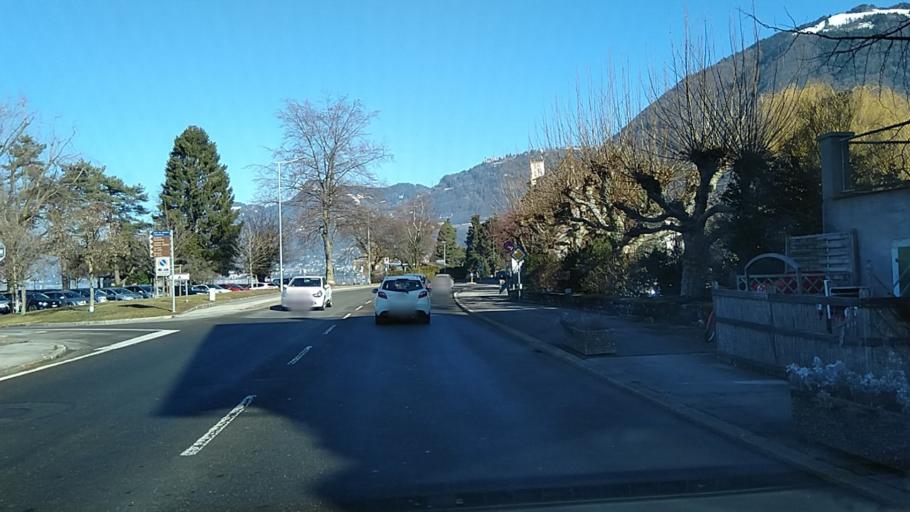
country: CH
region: Vaud
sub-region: Aigle District
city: Villeneuve
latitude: 46.3950
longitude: 6.9220
